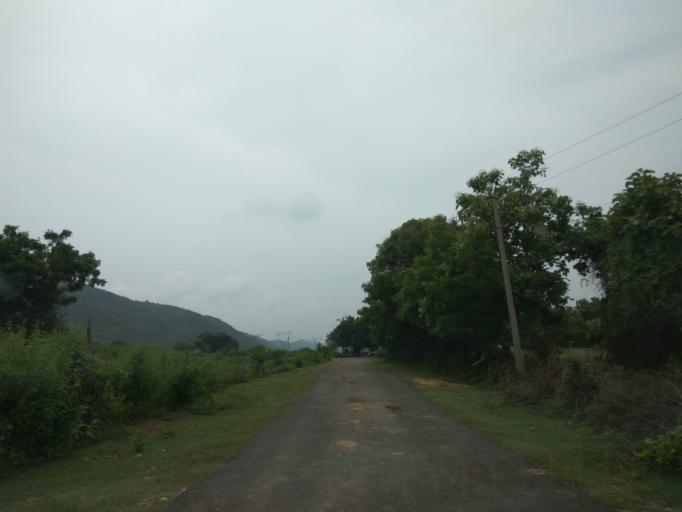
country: IN
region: Andhra Pradesh
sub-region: Prakasam
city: Cumbum
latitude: 15.4459
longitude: 79.0800
